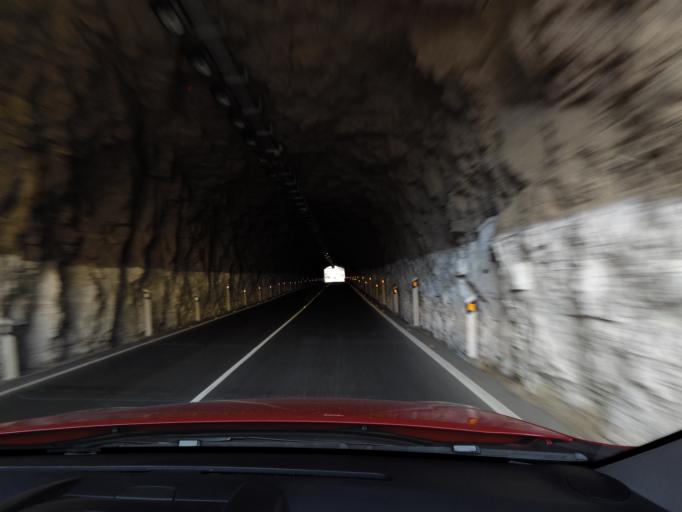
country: ES
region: Canary Islands
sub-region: Provincia de Las Palmas
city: Puerto Rico
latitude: 27.8039
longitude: -15.7372
